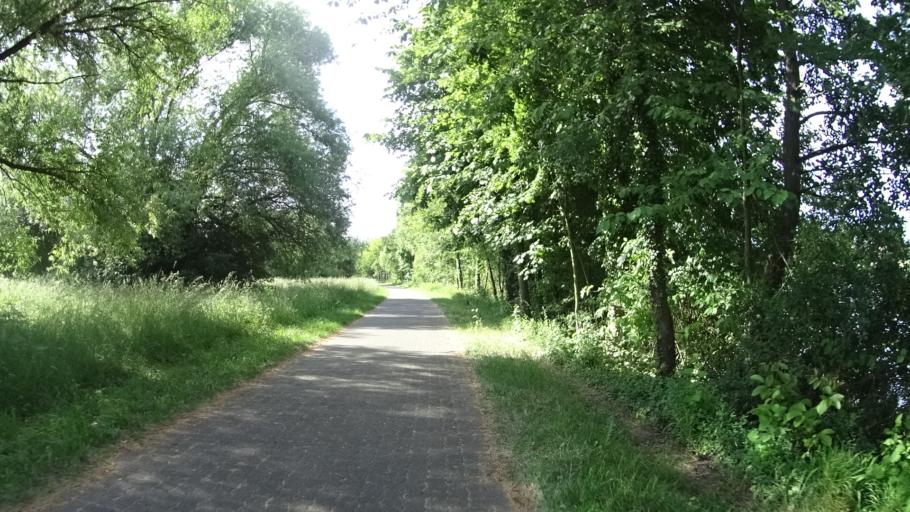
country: DE
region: Bavaria
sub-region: Regierungsbezirk Unterfranken
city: Stockstadt am Main
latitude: 49.9837
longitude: 9.0663
